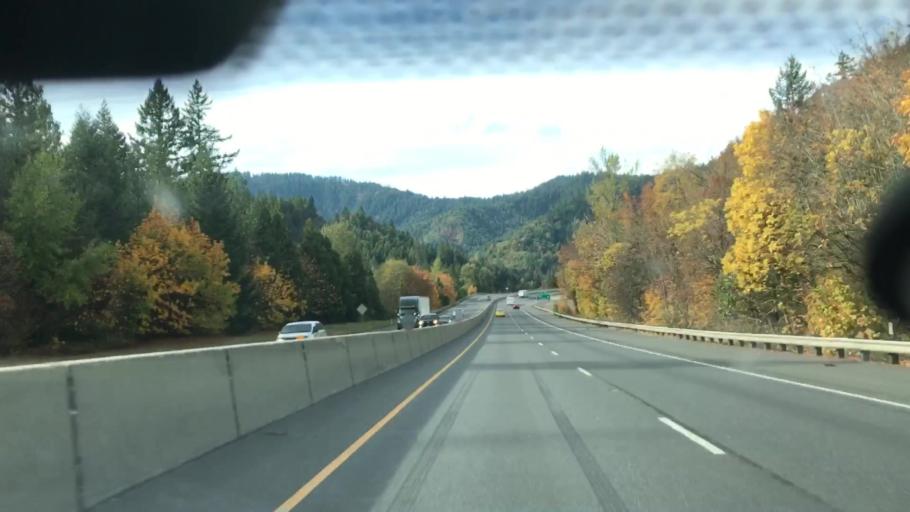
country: US
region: Oregon
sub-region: Josephine County
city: Merlin
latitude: 42.6852
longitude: -123.3891
